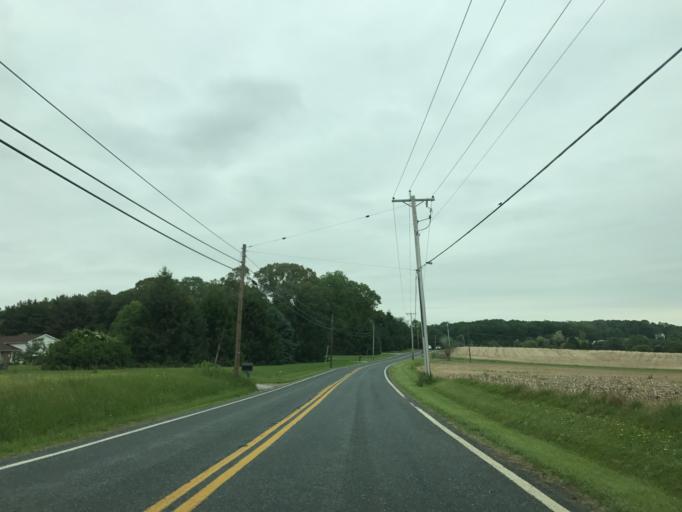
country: US
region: Pennsylvania
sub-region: York County
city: New Freedom
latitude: 39.6782
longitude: -76.7225
